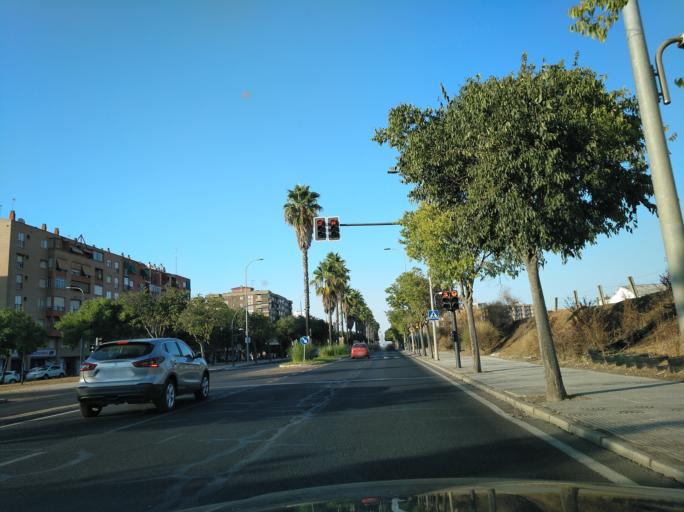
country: ES
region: Extremadura
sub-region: Provincia de Badajoz
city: Badajoz
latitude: 38.8626
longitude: -6.9850
